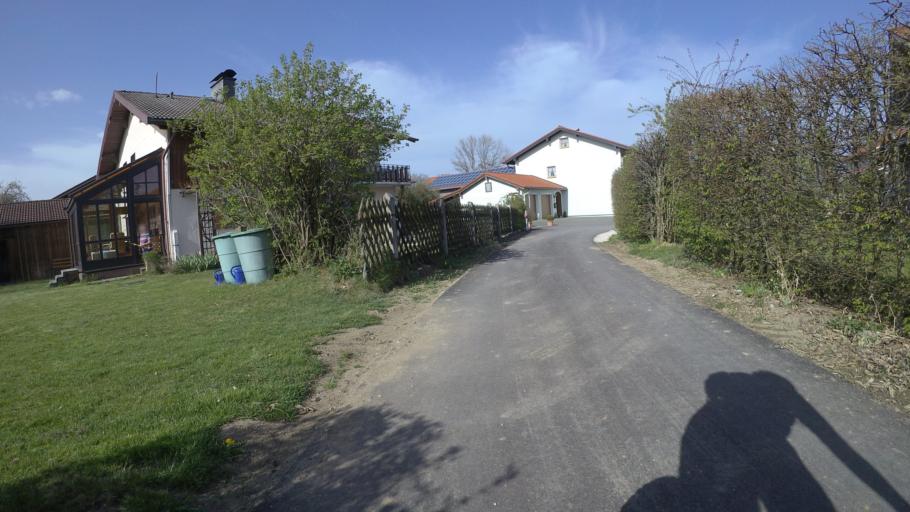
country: DE
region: Bavaria
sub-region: Upper Bavaria
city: Nussdorf
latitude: 47.9282
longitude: 12.6036
